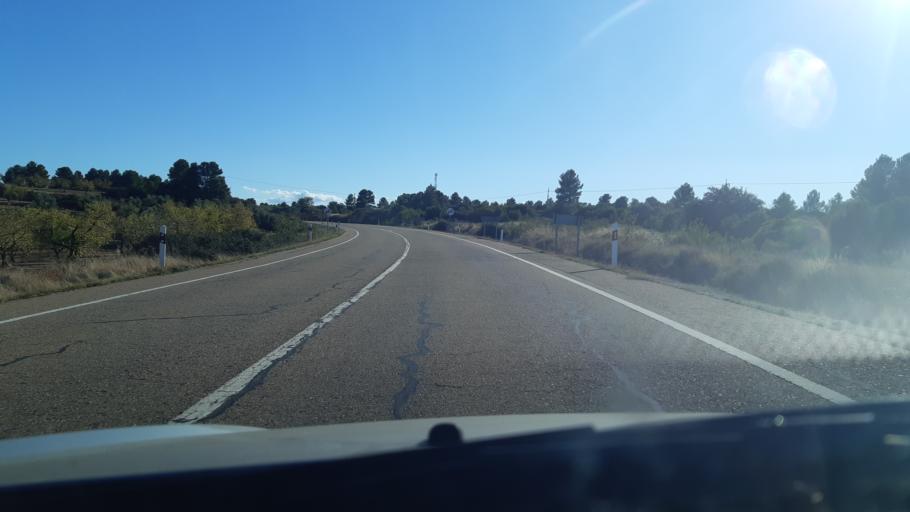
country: ES
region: Aragon
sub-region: Provincia de Teruel
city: Valdealgorfa
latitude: 40.9617
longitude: -0.0158
